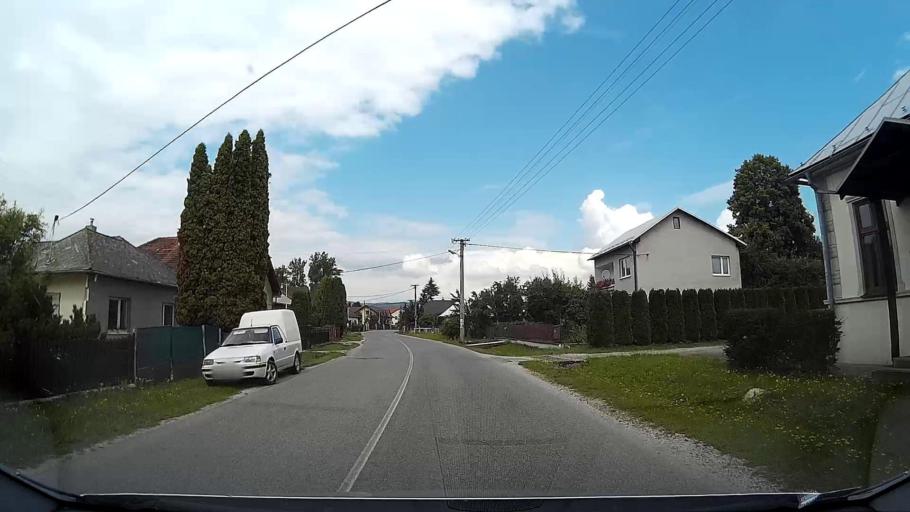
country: SK
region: Presovsky
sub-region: Okres Poprad
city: Poprad
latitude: 48.9806
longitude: 20.3899
